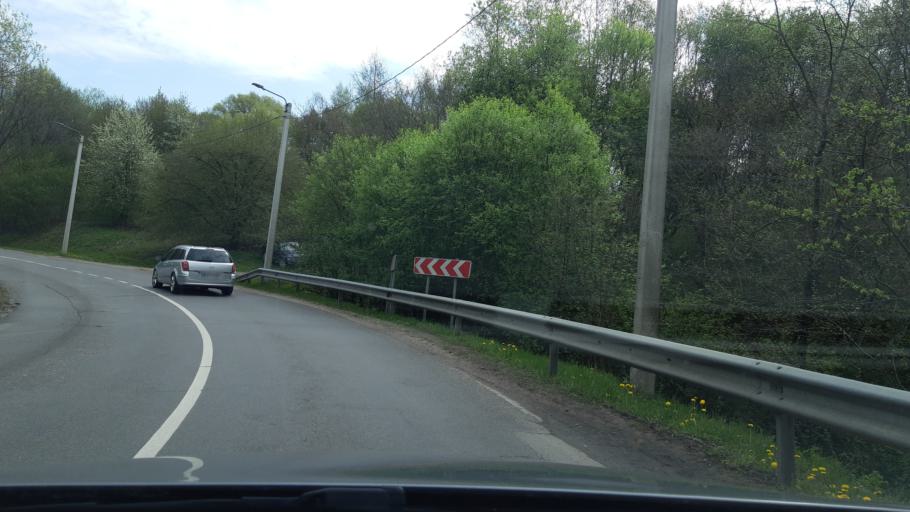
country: LT
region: Kauno apskritis
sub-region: Kaunas
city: Silainiai
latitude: 54.9225
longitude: 23.8622
